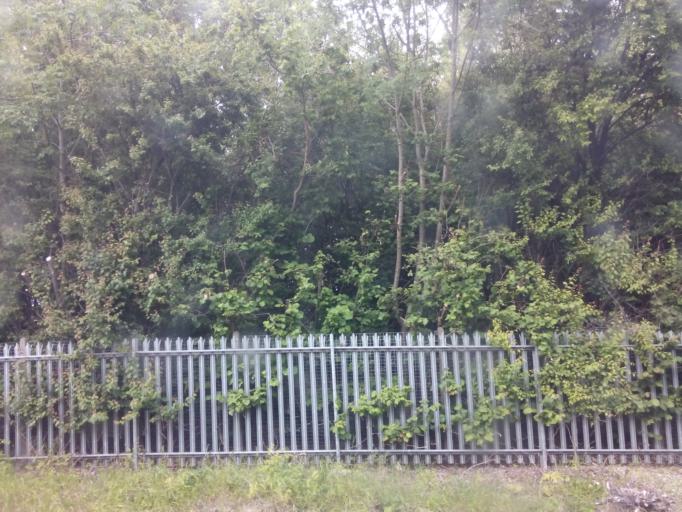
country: GB
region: England
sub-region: South Tyneside
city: Jarrow
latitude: 54.9750
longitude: -1.4658
